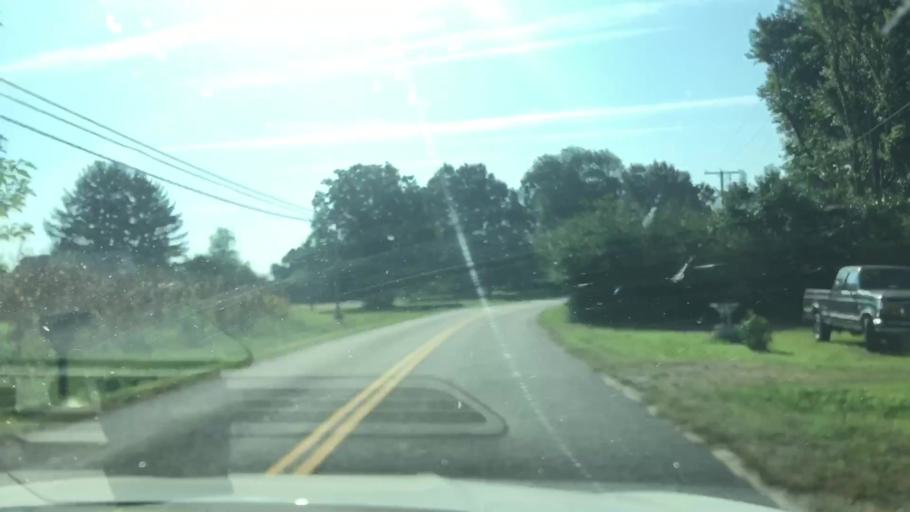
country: US
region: Virginia
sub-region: Richmond County
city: Warsaw
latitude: 37.8868
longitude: -76.6269
